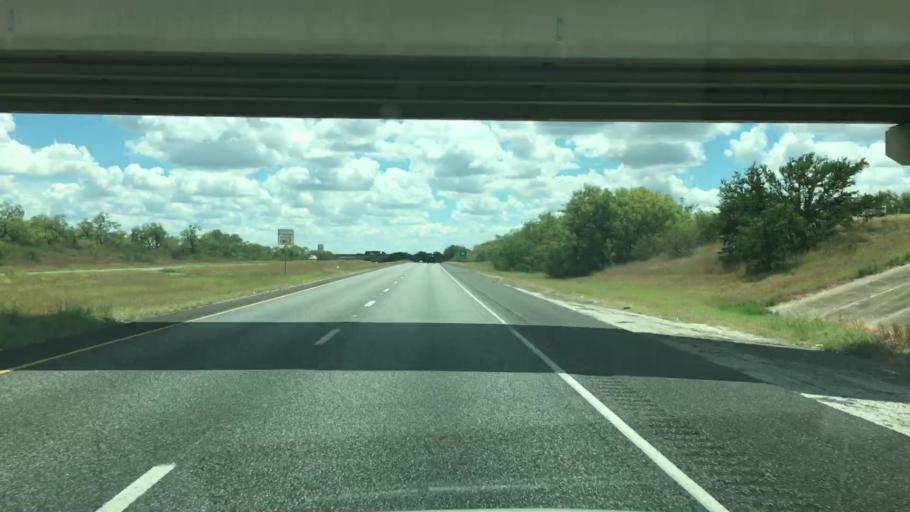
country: US
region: Texas
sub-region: Atascosa County
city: Pleasanton
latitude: 28.9164
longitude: -98.4350
